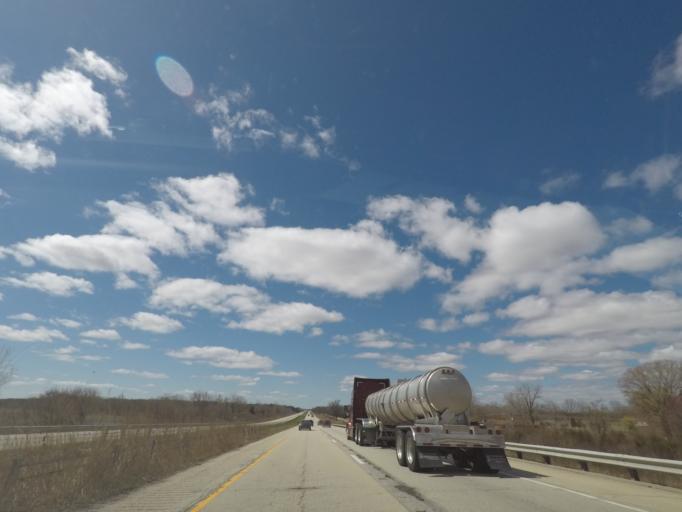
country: US
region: Illinois
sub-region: Grundy County
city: Central City
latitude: 41.2225
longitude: -88.2816
